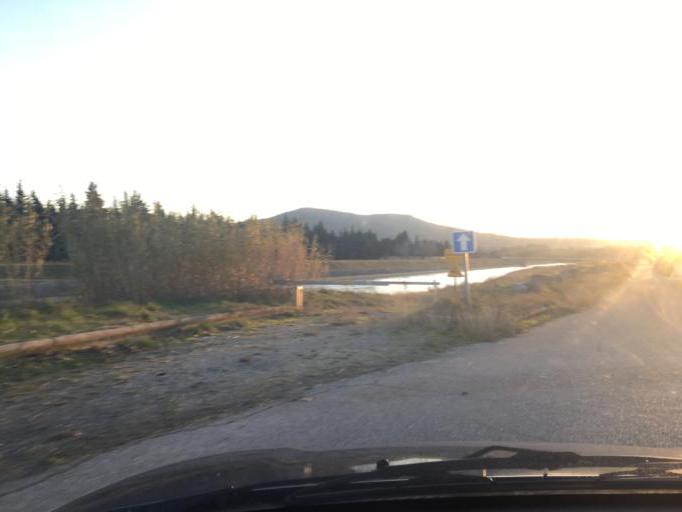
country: FR
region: Provence-Alpes-Cote d'Azur
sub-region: Departement des Bouches-du-Rhone
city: Mallemort
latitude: 43.7242
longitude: 5.1854
